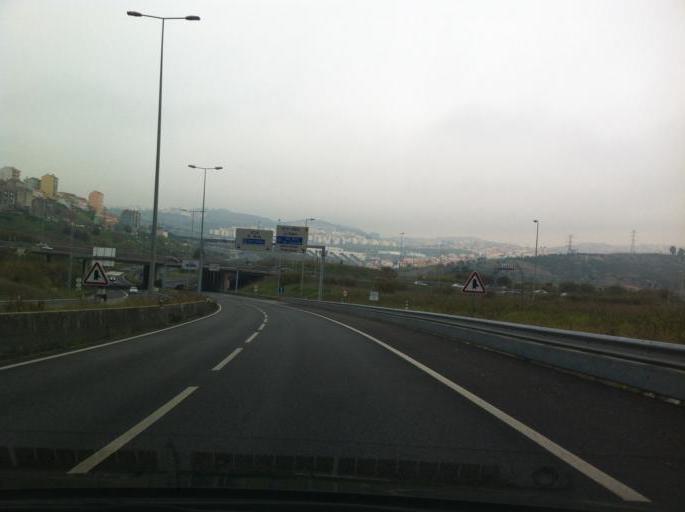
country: PT
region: Lisbon
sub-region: Odivelas
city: Pontinha
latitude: 38.7679
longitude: -9.2070
